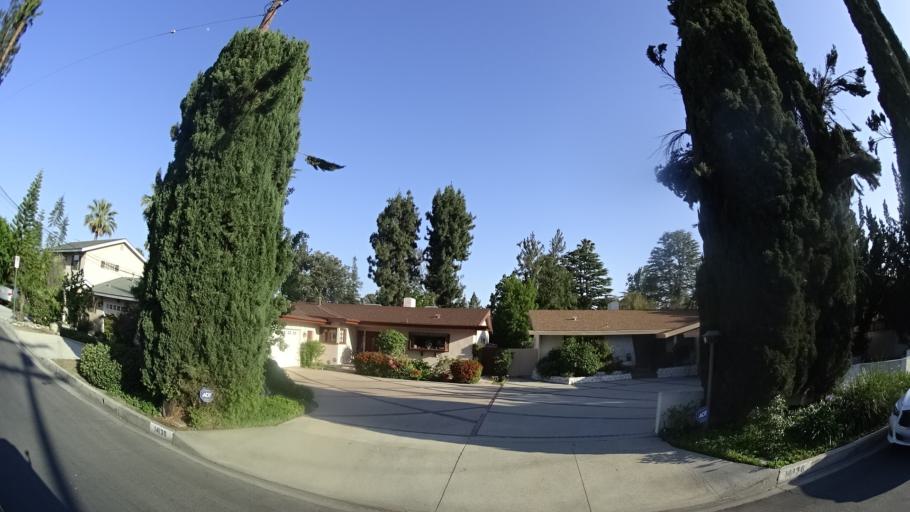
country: US
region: California
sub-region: Los Angeles County
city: Van Nuys
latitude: 34.1703
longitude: -118.4413
